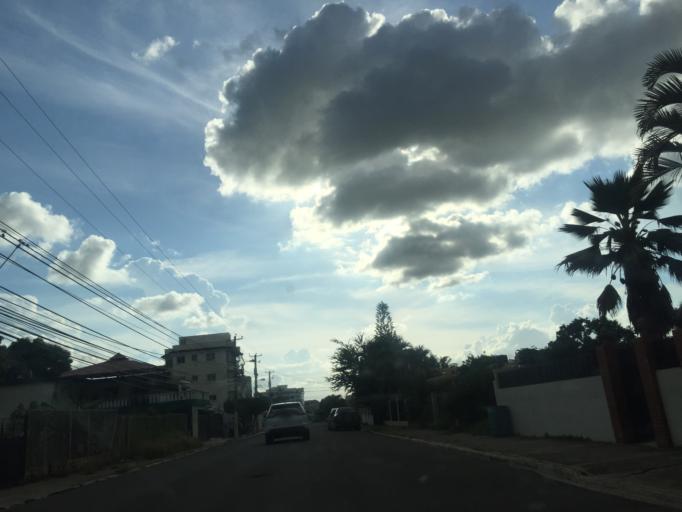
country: DO
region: Santiago
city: Santiago de los Caballeros
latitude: 19.4345
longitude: -70.6633
